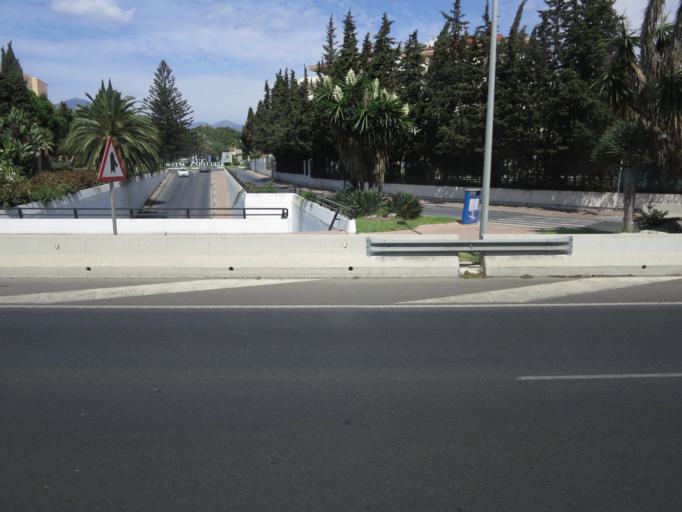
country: ES
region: Andalusia
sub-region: Provincia de Malaga
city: Marbella
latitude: 36.4876
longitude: -4.9640
